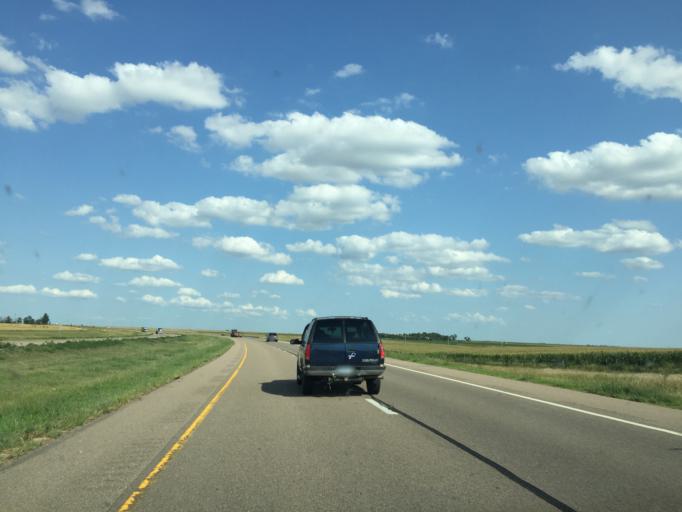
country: US
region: Kansas
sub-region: Trego County
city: WaKeeney
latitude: 39.0250
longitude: -100.1716
